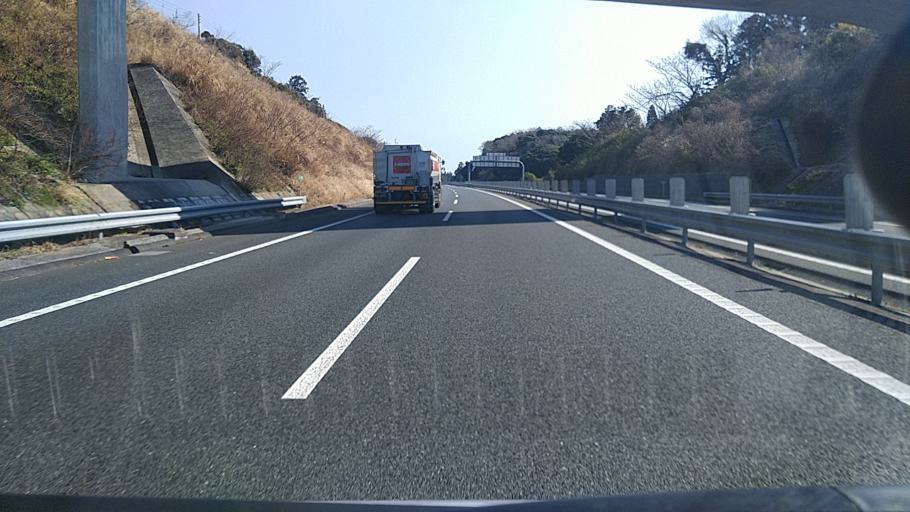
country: JP
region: Chiba
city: Kisarazu
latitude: 35.3671
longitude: 139.9897
